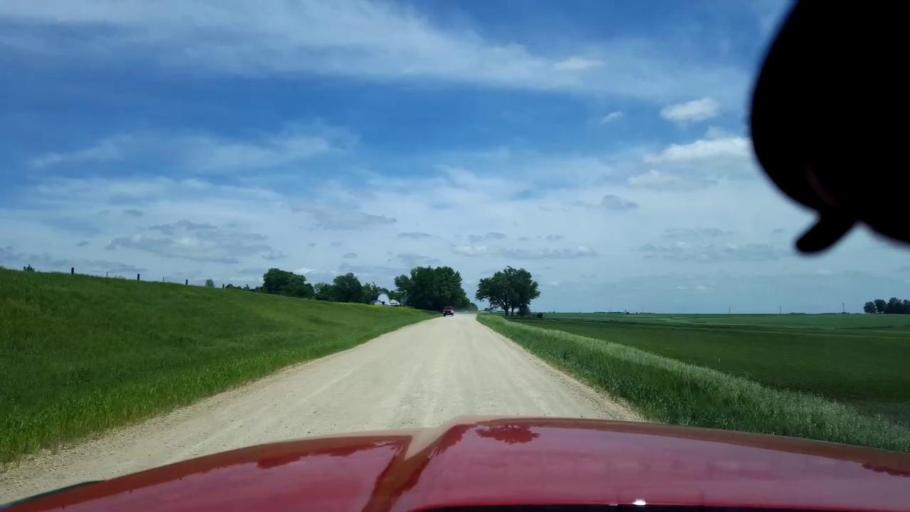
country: US
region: Iowa
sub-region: Linn County
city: Lisbon
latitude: 41.9557
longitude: -91.3640
